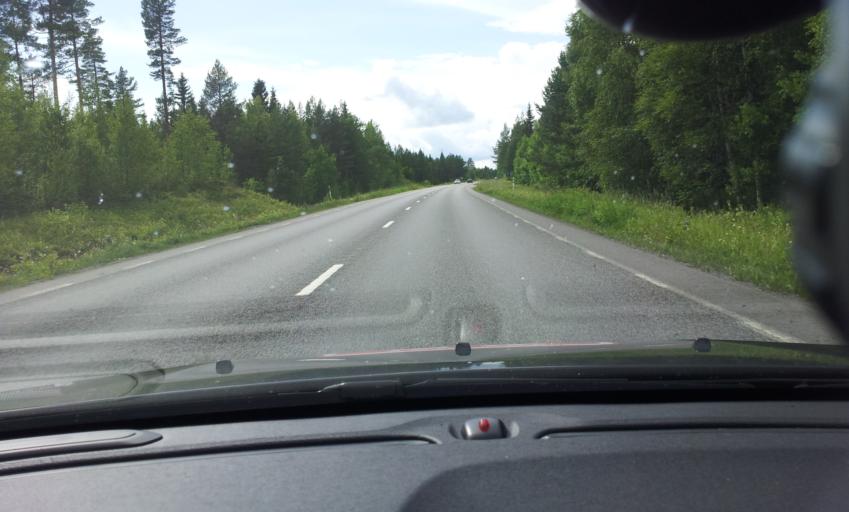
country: SE
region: Jaemtland
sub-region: Krokoms Kommun
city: Krokom
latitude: 63.3131
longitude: 14.1338
